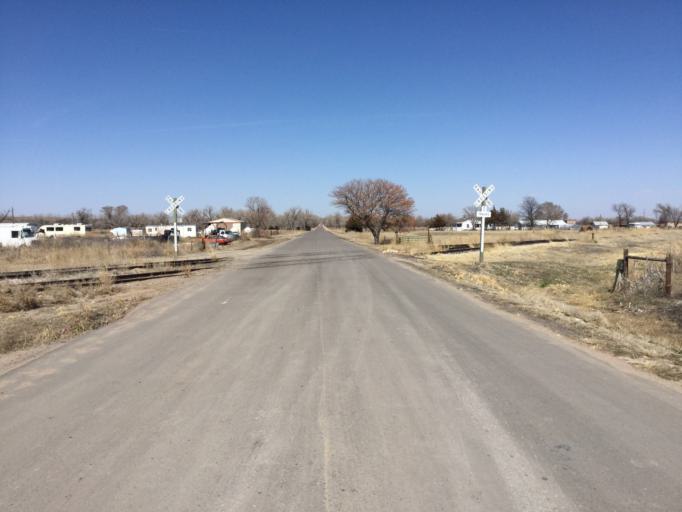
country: US
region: Kansas
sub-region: Cheyenne County
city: Saint Francis
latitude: 39.7811
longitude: -101.8002
